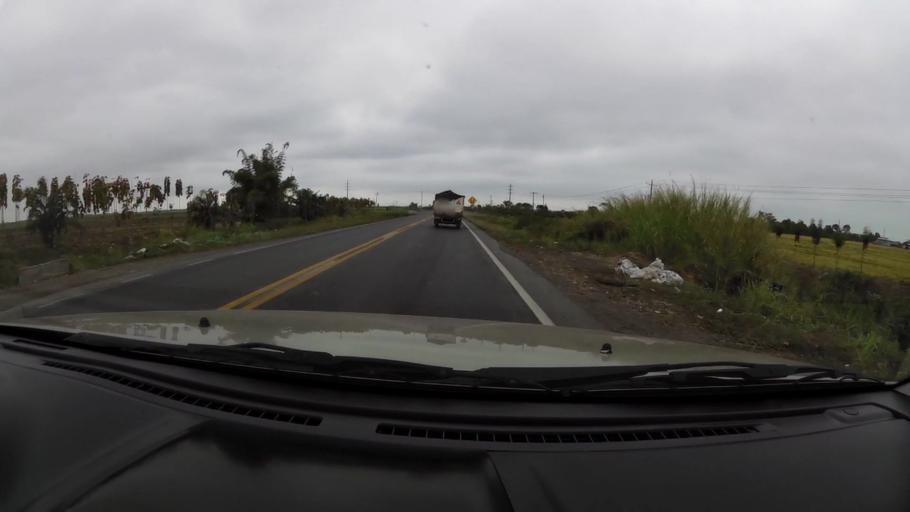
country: EC
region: Guayas
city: Naranjal
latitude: -2.5010
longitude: -79.5944
